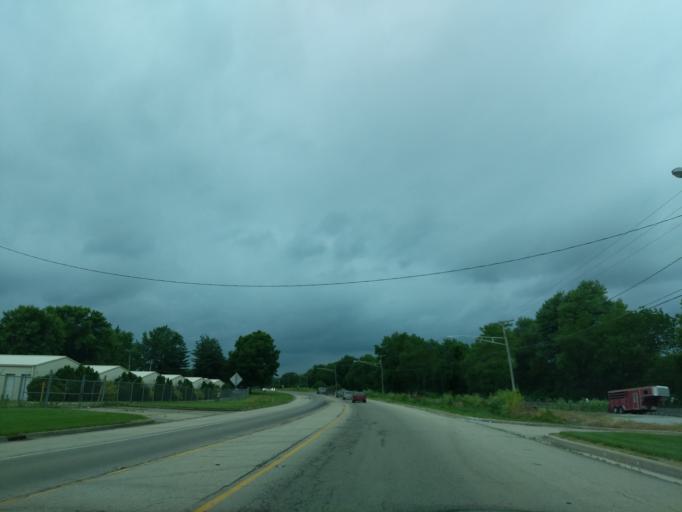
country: US
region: Indiana
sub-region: Madison County
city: Chesterfield
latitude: 40.1140
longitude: -85.5781
